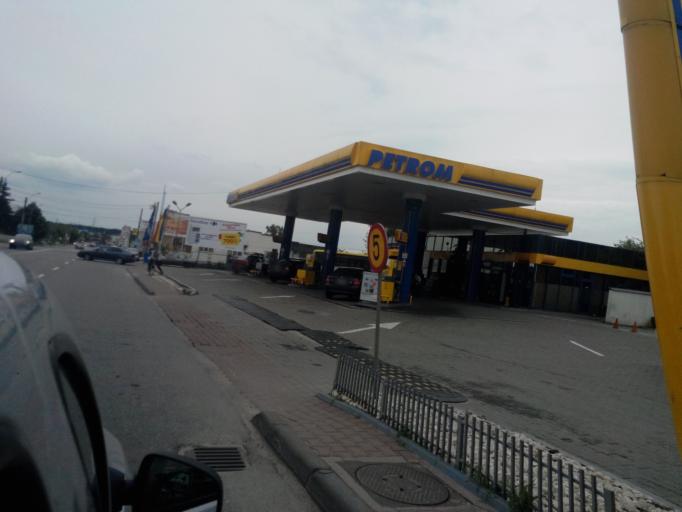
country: RO
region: Arges
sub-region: Comuna Bascov
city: Bascov
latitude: 44.8900
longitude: 24.8225
